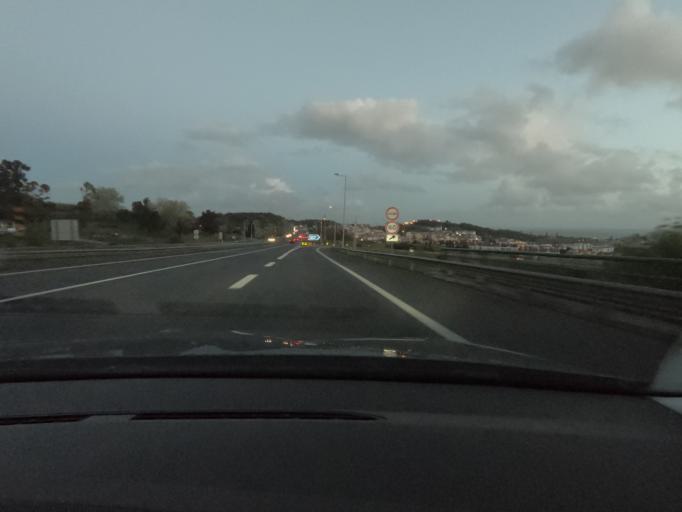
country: PT
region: Lisbon
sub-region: Oeiras
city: Quejas
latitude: 38.7188
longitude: -9.2708
